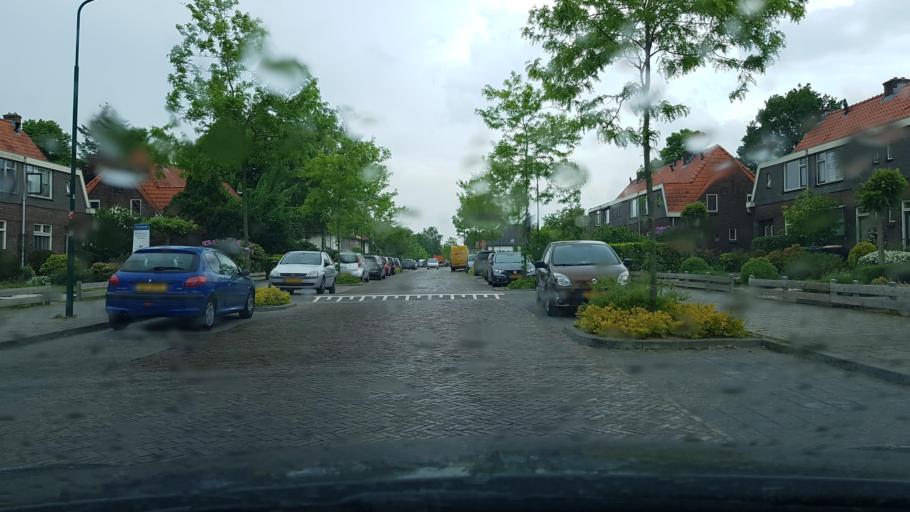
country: NL
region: Utrecht
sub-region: Gemeente Soest
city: Soest
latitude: 52.1799
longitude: 5.2840
